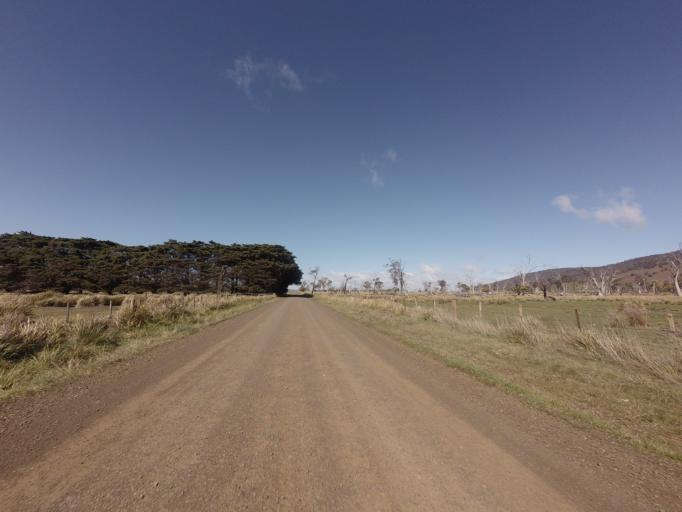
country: AU
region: Tasmania
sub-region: Northern Midlands
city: Evandale
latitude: -41.9434
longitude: 147.4284
